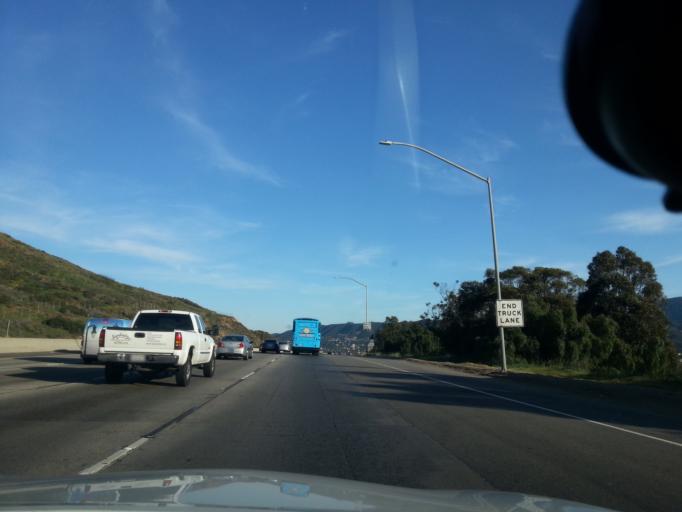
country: US
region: California
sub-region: Ventura County
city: Casa Conejo
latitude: 34.1981
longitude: -118.9543
